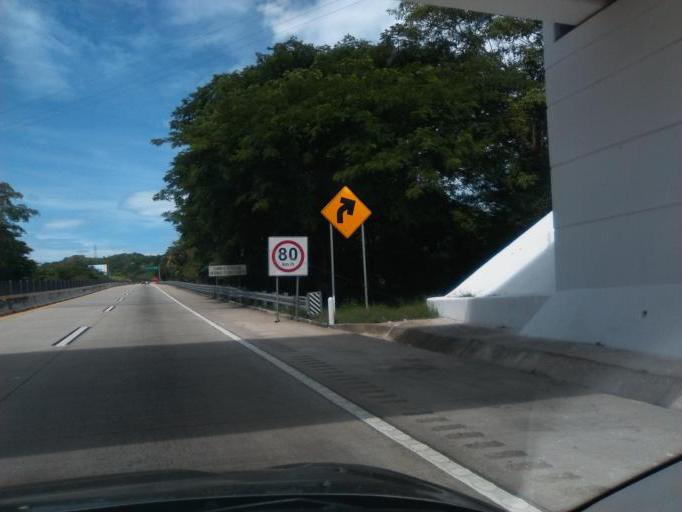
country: MX
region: Guerrero
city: Tierra Colorada
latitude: 17.1652
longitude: -99.5536
